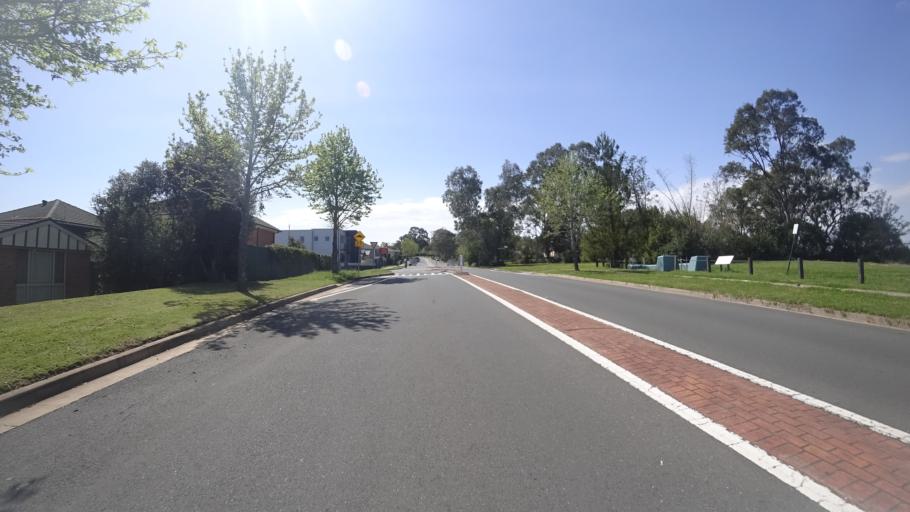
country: AU
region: New South Wales
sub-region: Campbelltown Municipality
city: Glenfield
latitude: -33.9589
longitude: 150.9044
